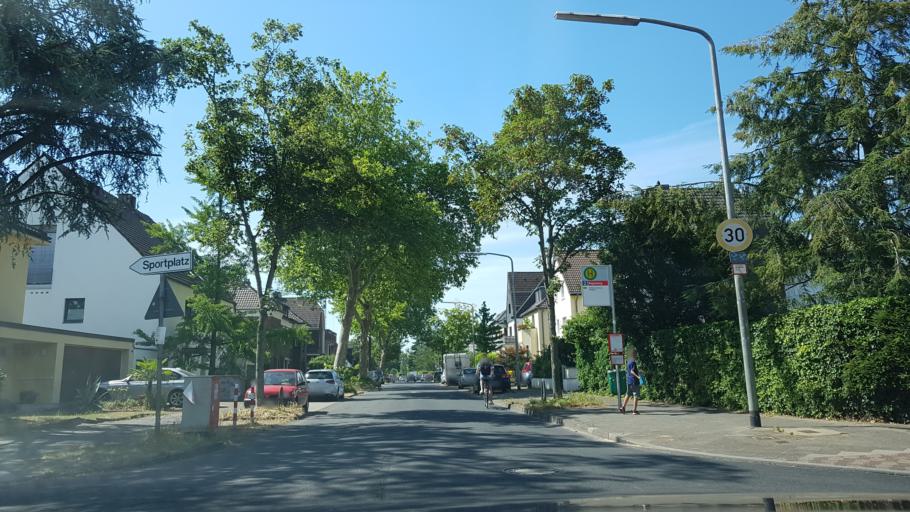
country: DE
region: North Rhine-Westphalia
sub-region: Regierungsbezirk Dusseldorf
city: Meerbusch
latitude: 51.2771
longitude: 6.7314
